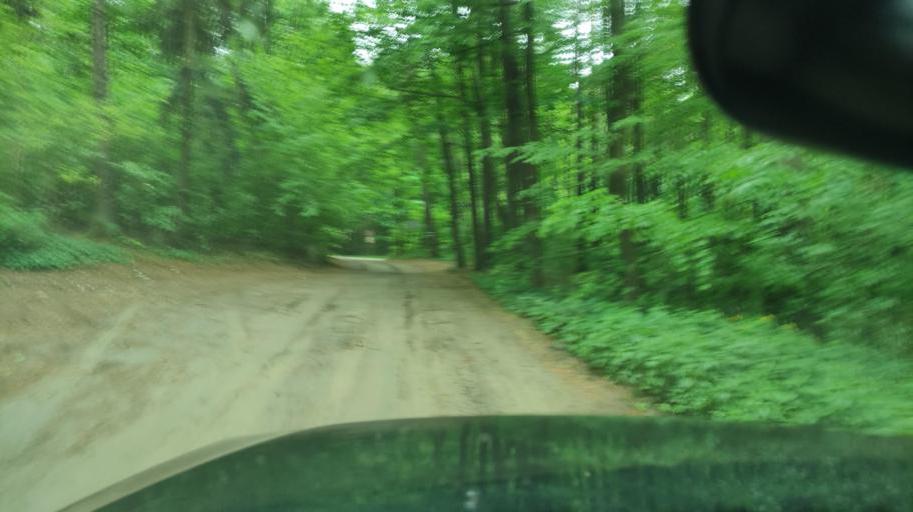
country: PL
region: Warmian-Masurian Voivodeship
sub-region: Powiat olsztynski
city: Olsztyn
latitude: 53.7586
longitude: 20.5205
